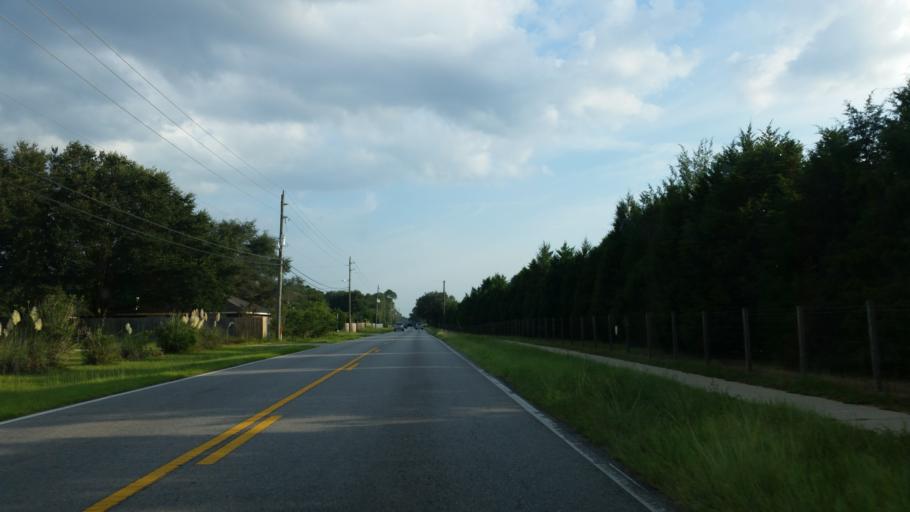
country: US
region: Florida
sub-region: Santa Rosa County
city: Pace
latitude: 30.6239
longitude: -87.1315
